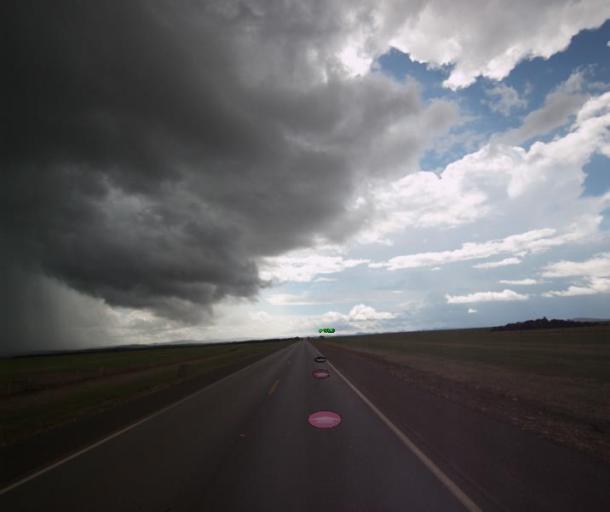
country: BR
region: Goias
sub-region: Uruacu
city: Uruacu
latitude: -14.6484
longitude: -49.1682
